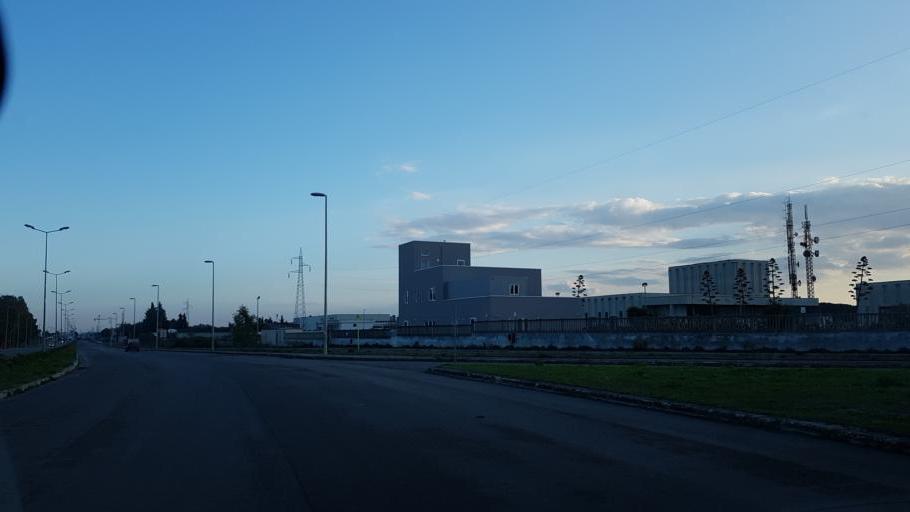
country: IT
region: Apulia
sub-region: Provincia di Lecce
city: Surbo
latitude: 40.3840
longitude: 18.1186
